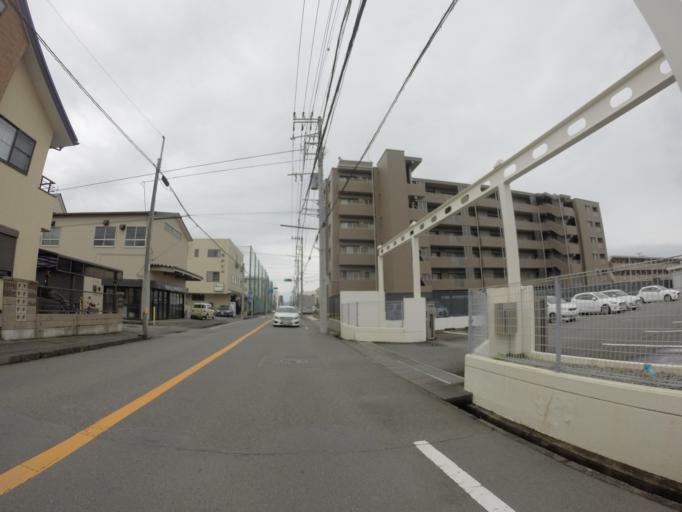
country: JP
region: Shizuoka
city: Numazu
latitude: 35.1146
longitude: 138.8526
